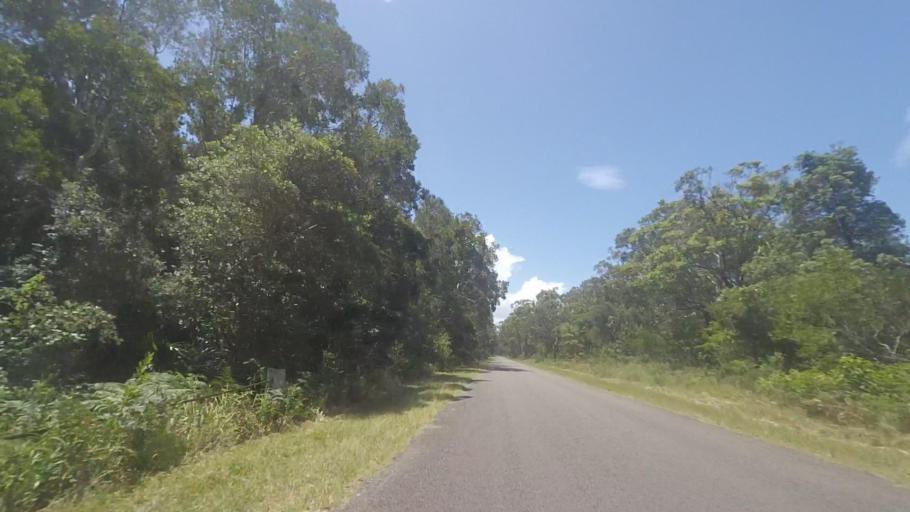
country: AU
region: New South Wales
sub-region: Great Lakes
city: Bulahdelah
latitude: -32.5333
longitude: 152.3211
